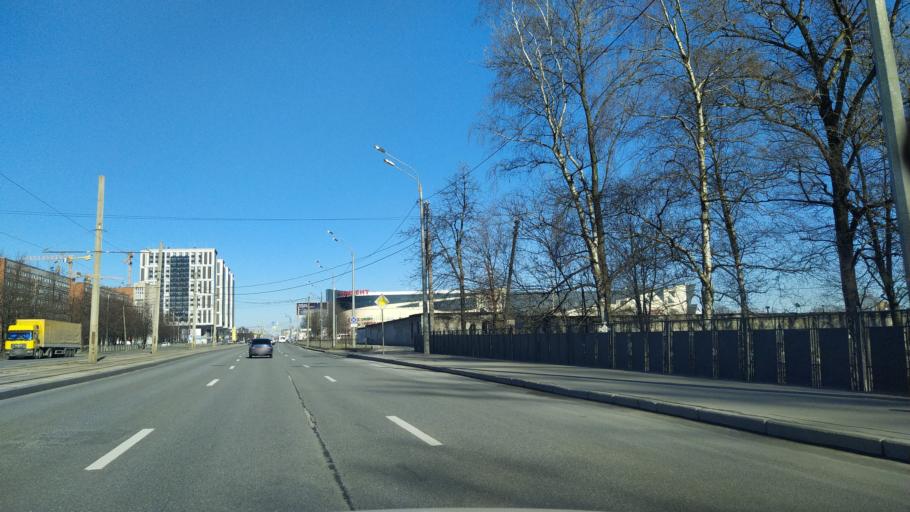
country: RU
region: St.-Petersburg
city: Kupchino
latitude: 59.8818
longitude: 30.3622
